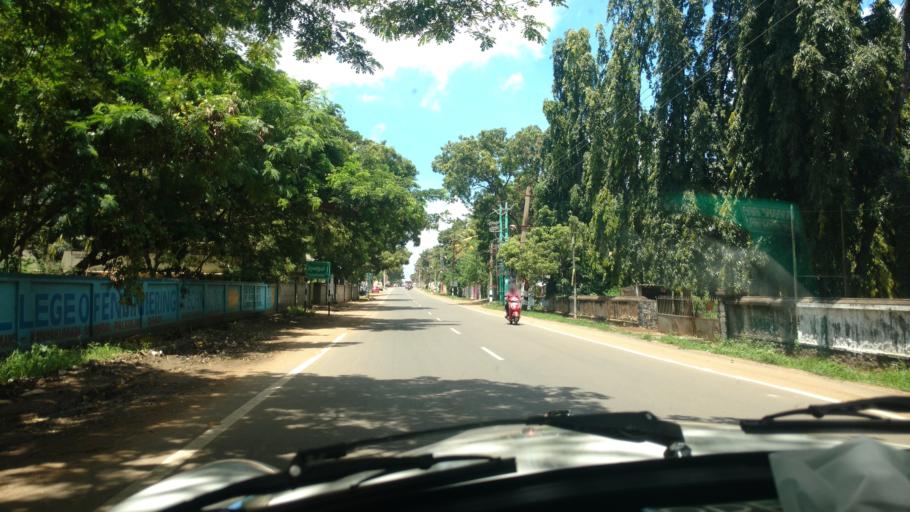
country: IN
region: Tamil Nadu
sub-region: Kanniyakumari
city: Nagercoil
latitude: 8.1829
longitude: 77.4135
